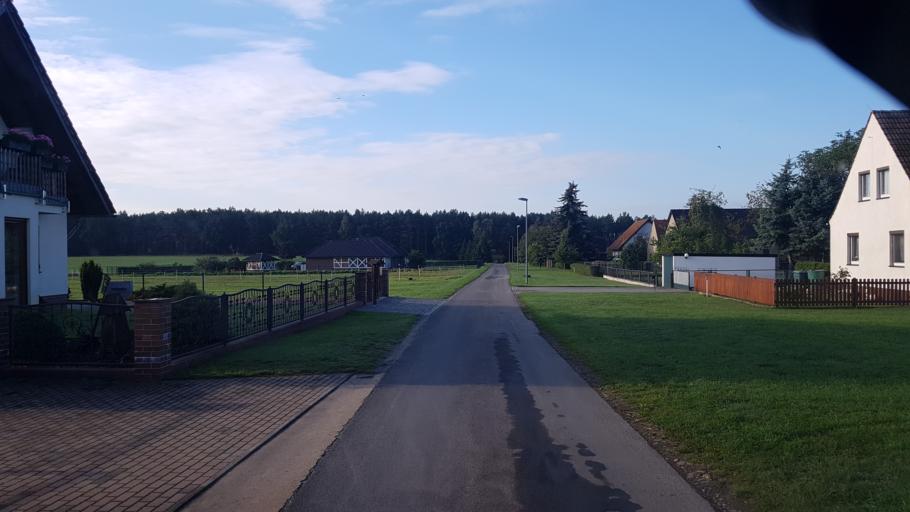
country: DE
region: Brandenburg
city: Bronkow
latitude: 51.6749
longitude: 13.8920
